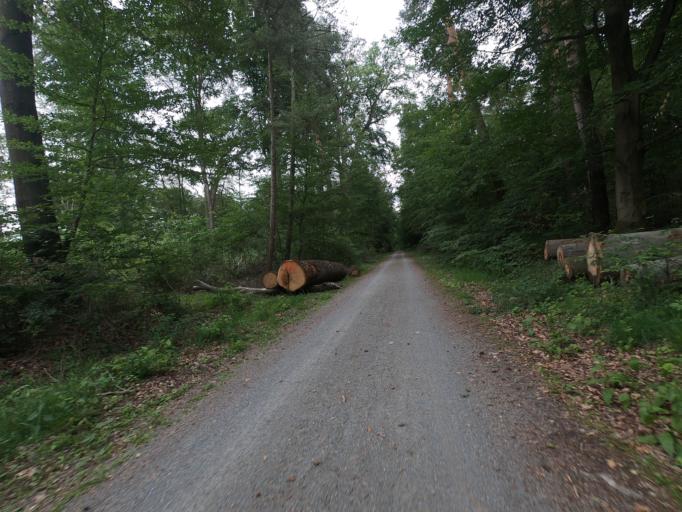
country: DE
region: Hesse
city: Morfelden-Walldorf
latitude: 50.0287
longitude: 8.6248
